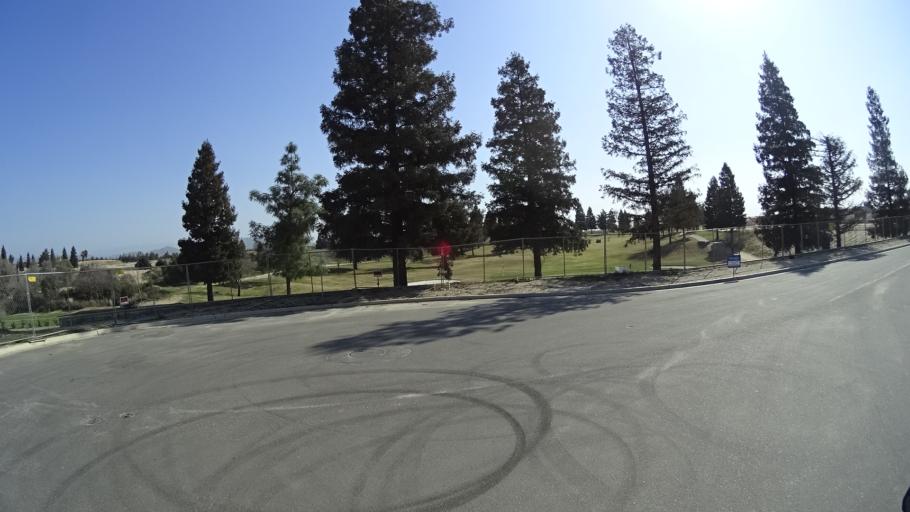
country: US
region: California
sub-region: Fresno County
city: Clovis
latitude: 36.8995
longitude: -119.7385
